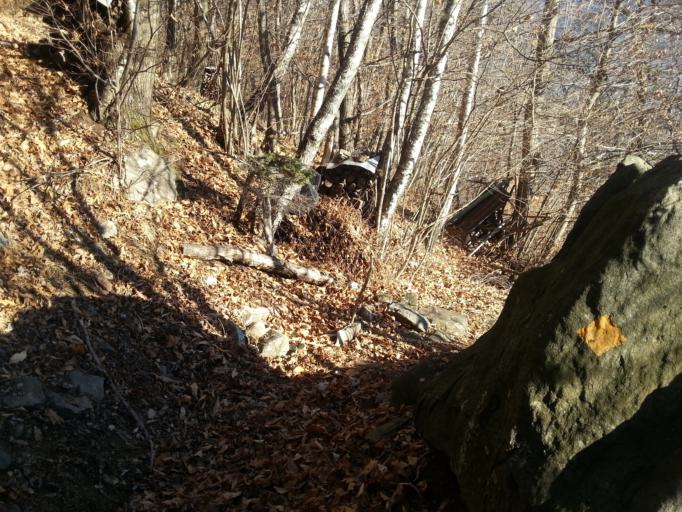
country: CH
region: Ticino
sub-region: Bellinzona District
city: Cadenazzo
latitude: 46.1220
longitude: 8.9545
